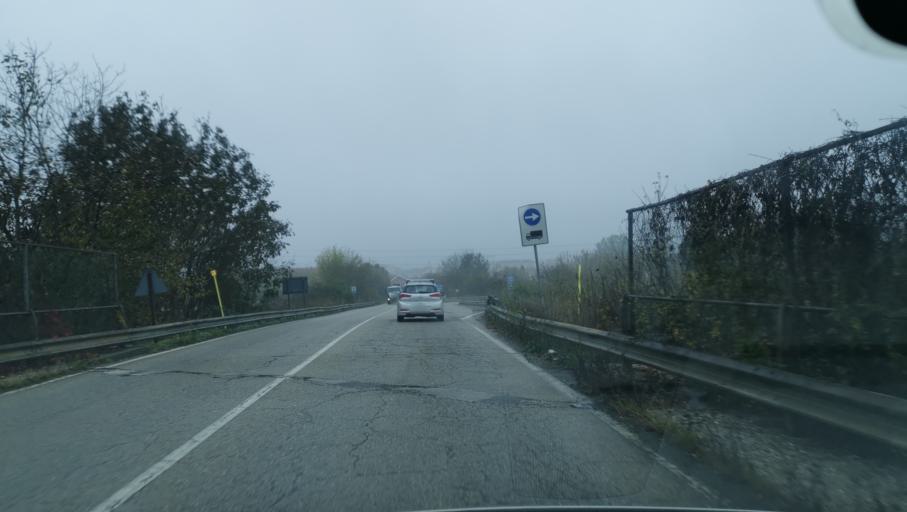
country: IT
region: Piedmont
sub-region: Provincia di Torino
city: Settimo Torinese
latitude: 45.1321
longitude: 7.7819
